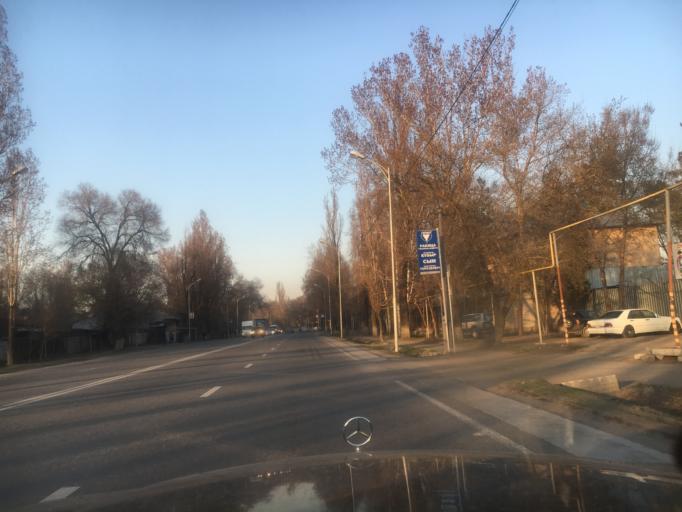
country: KZ
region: Almaty Oblysy
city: Pervomayskiy
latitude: 43.3530
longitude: 76.9745
